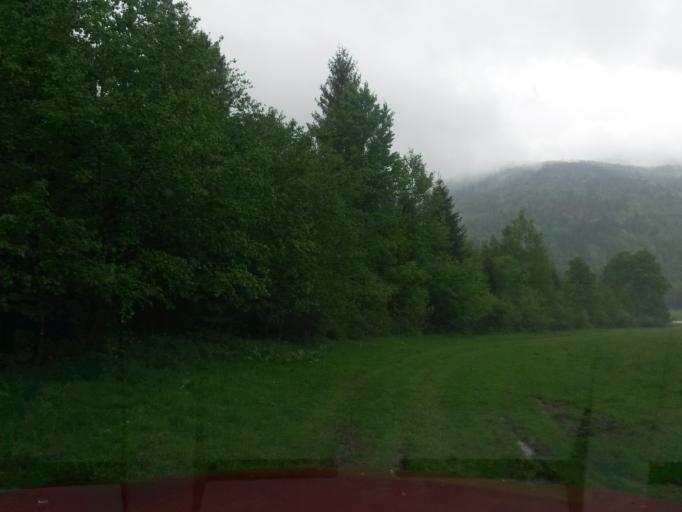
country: SK
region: Kosicky
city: Medzev
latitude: 48.7872
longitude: 20.7754
